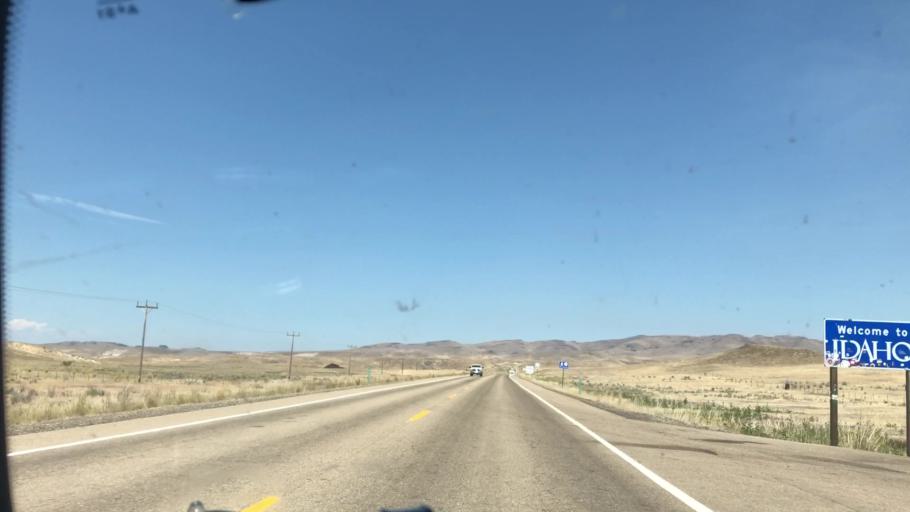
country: US
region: Idaho
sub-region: Owyhee County
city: Marsing
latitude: 43.2516
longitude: -117.0253
